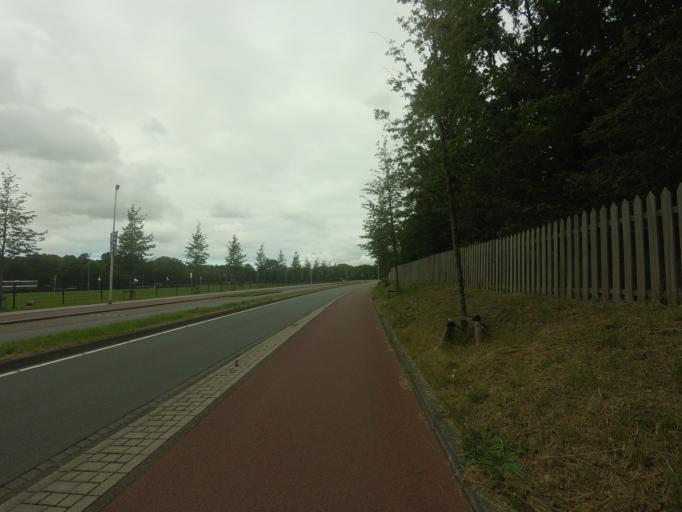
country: NL
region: North Holland
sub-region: Gemeente Bloemendaal
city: Bloemendaal
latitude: 52.4143
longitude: 4.6171
